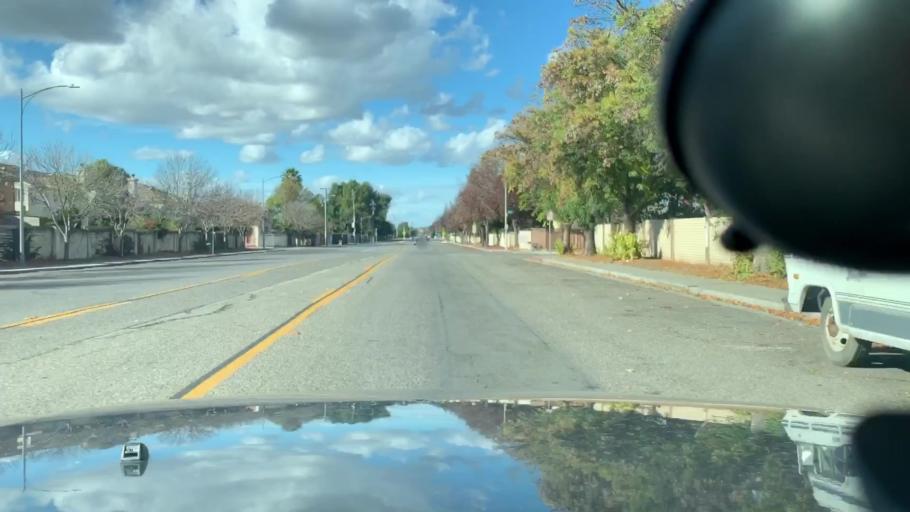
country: US
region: California
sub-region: Santa Clara County
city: Seven Trees
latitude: 37.3183
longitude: -121.8456
